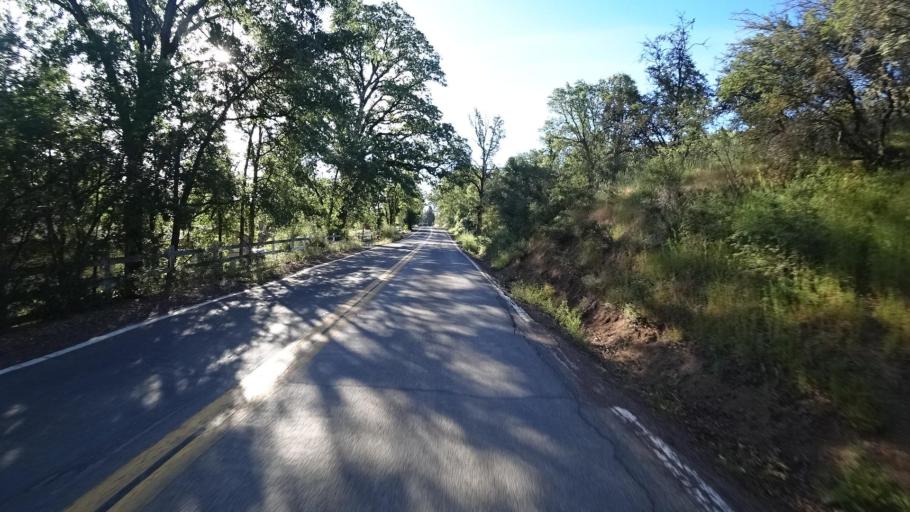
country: US
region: California
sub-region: Lake County
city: North Lakeport
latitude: 39.0958
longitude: -122.9690
